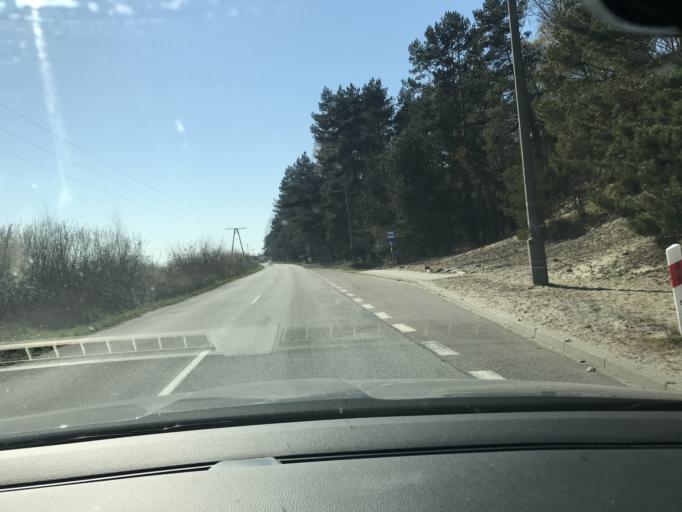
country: PL
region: Pomeranian Voivodeship
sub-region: Powiat nowodworski
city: Sztutowo
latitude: 54.3495
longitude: 19.2728
